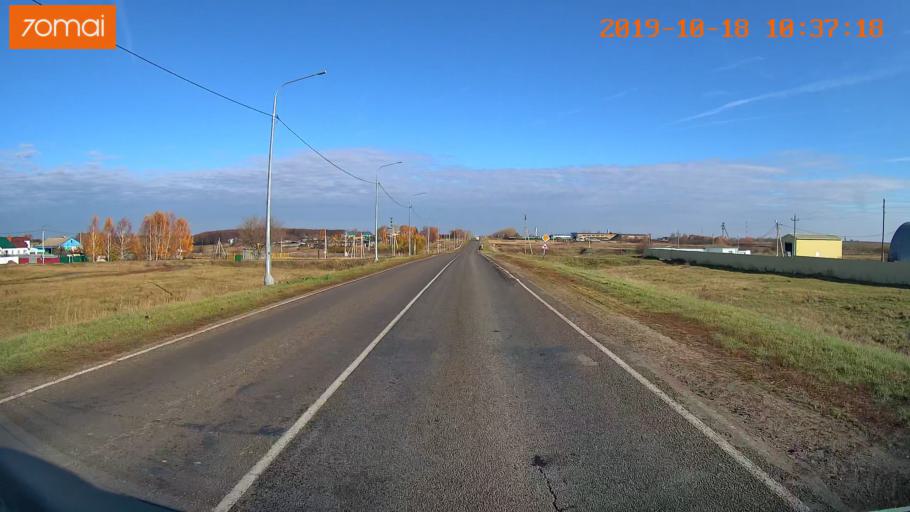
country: RU
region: Tula
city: Kurkino
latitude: 53.5605
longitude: 38.6311
